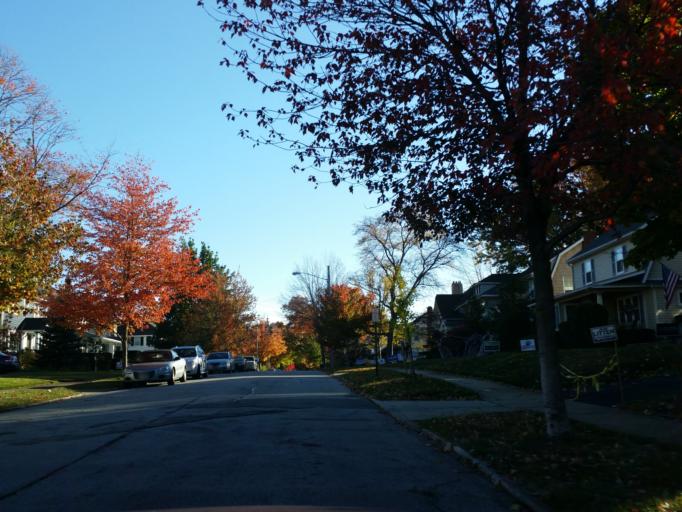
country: US
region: Ohio
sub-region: Cuyahoga County
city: Lakewood
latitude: 41.4818
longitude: -81.7842
